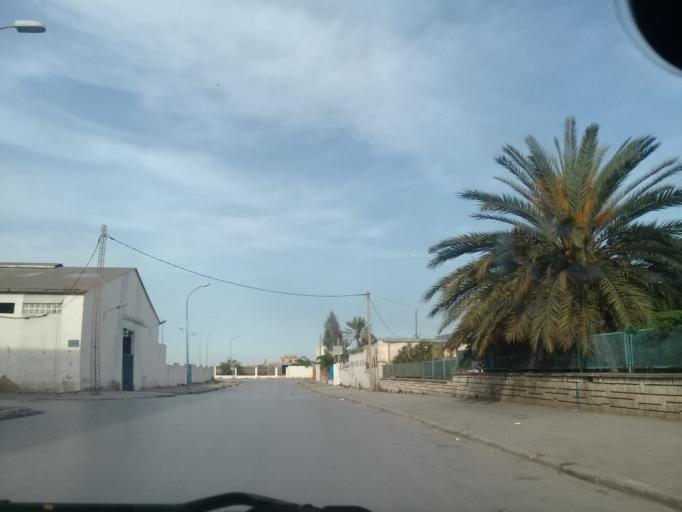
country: TN
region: Tunis
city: Tunis
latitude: 36.7904
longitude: 10.1865
